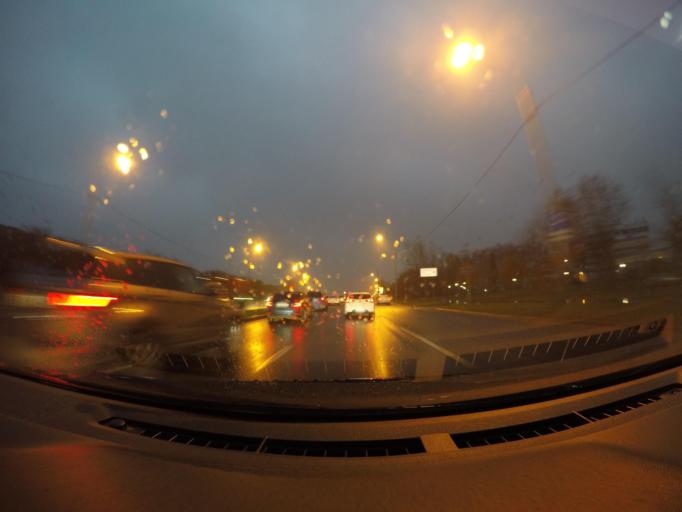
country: RU
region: Moscow
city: Kolomenskoye
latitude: 55.6662
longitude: 37.6506
